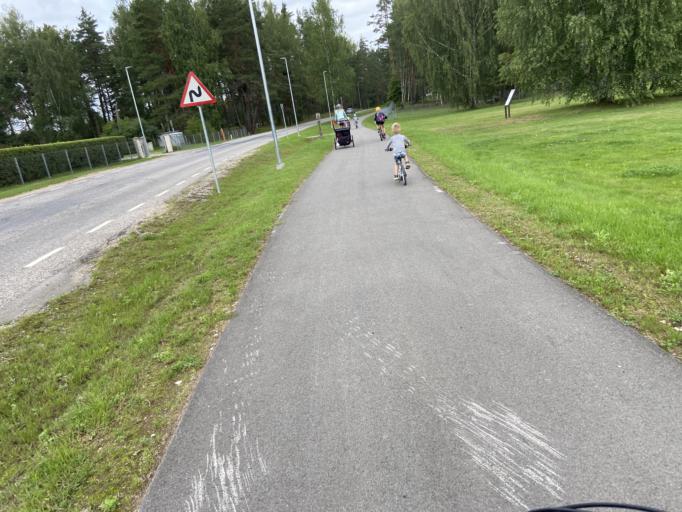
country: RU
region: Pskov
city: Pechory
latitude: 57.9390
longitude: 27.6529
